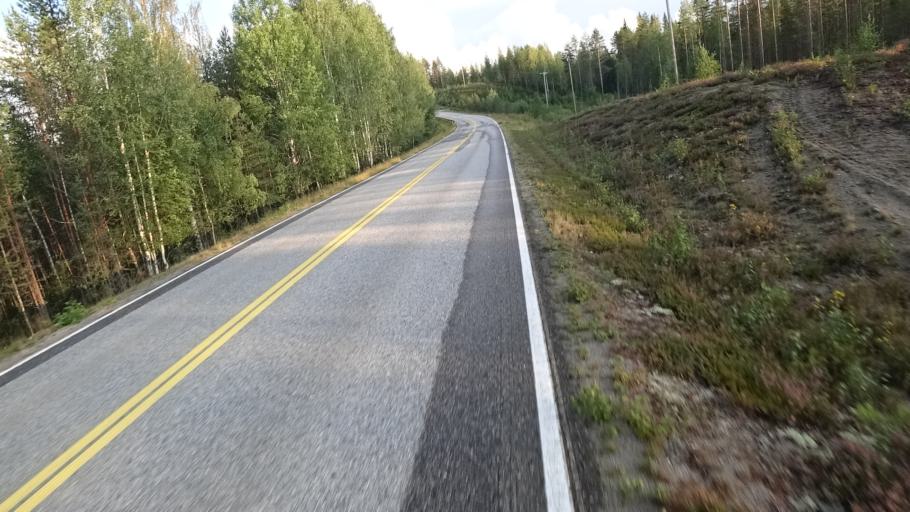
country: FI
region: North Karelia
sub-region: Joensuu
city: Ilomantsi
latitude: 62.6310
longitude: 31.0935
